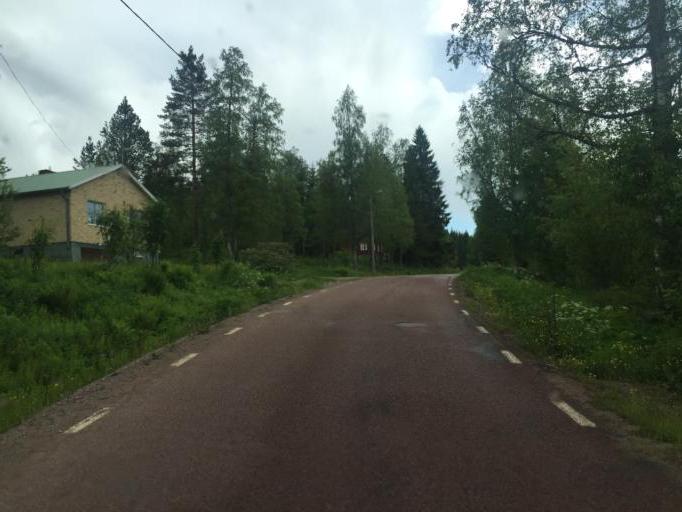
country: SE
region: Dalarna
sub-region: Malung-Saelens kommun
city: Malung
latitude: 60.3789
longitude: 13.8702
